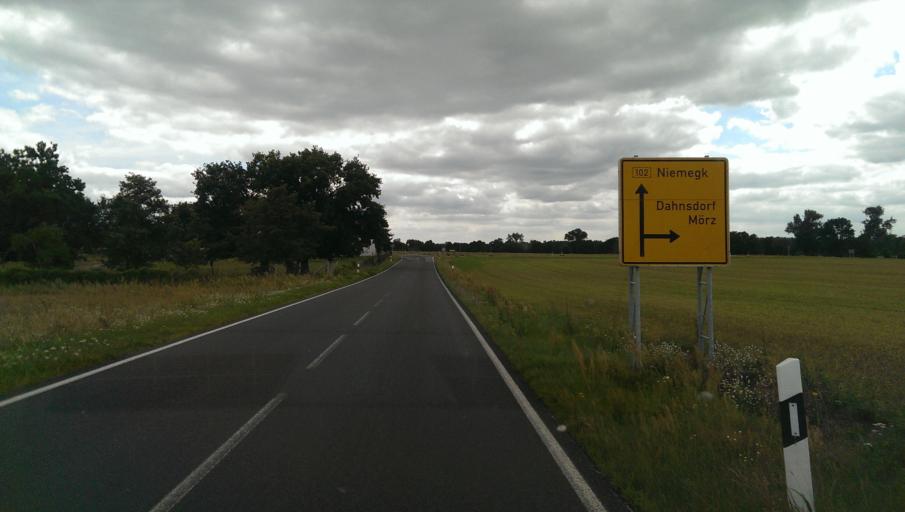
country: DE
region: Brandenburg
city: Niemegk
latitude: 52.1195
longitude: 12.7005
